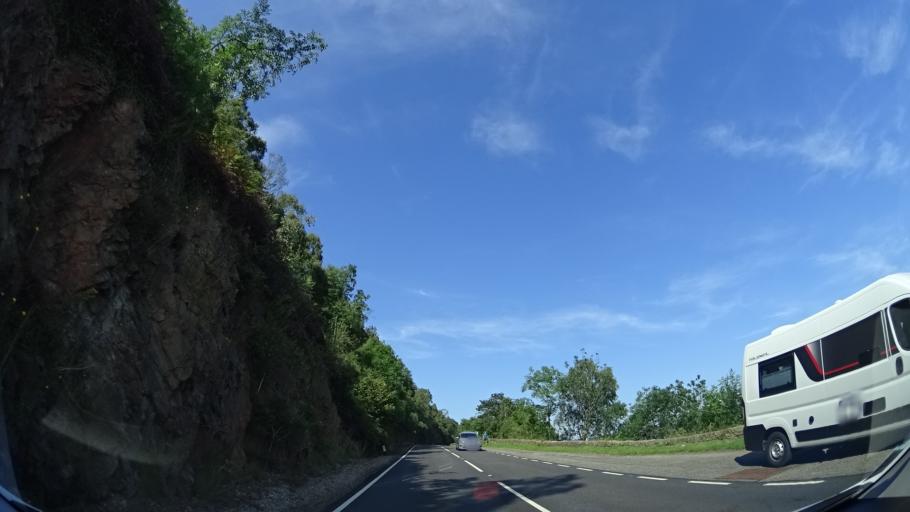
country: GB
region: Scotland
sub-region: Highland
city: Beauly
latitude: 57.3886
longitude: -4.3678
